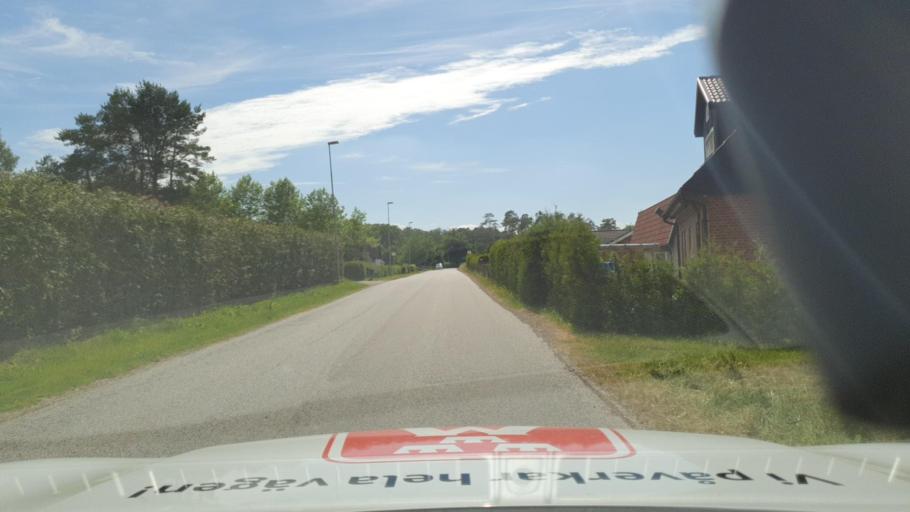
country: SE
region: Skane
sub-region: Sjobo Kommun
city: Sjoebo
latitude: 55.6299
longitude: 13.7251
